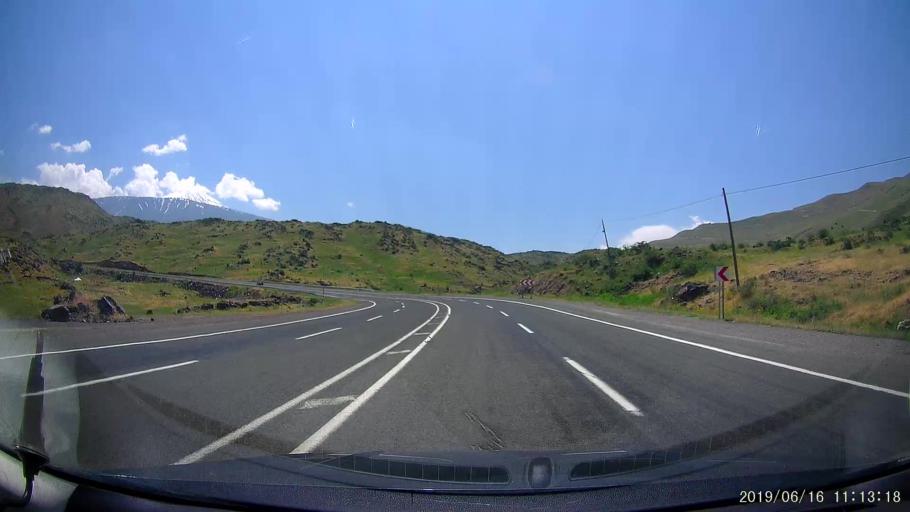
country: TR
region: Igdir
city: Igdir
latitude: 39.7857
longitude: 44.1357
